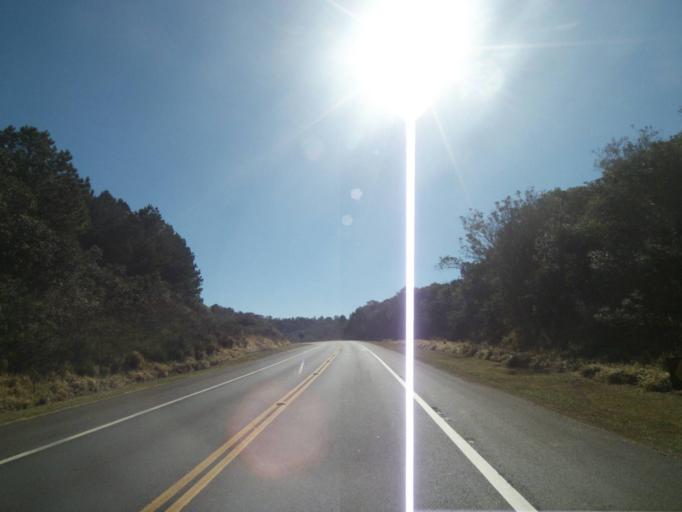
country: BR
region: Parana
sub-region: Tibagi
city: Tibagi
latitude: -24.6917
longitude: -50.5810
